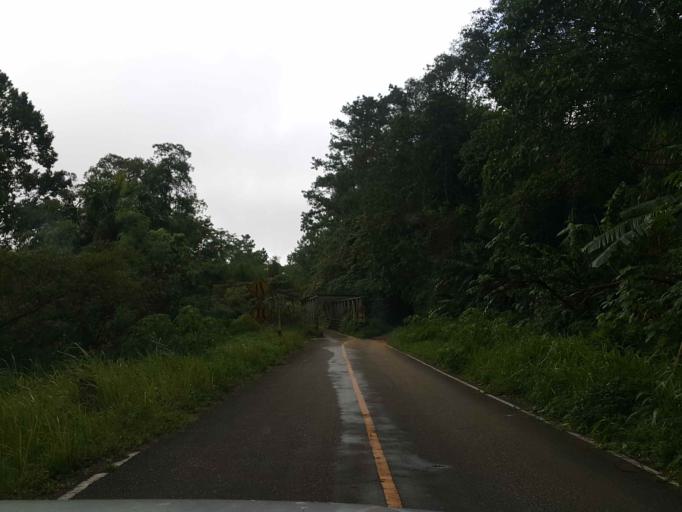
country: TH
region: Tak
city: Tak
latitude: 16.7814
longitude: 98.9271
